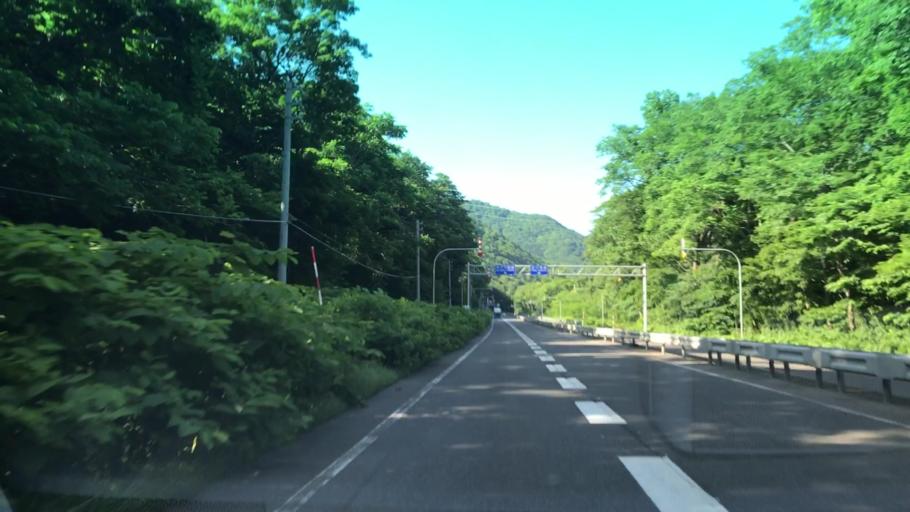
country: JP
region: Hokkaido
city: Iwanai
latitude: 43.0120
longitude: 140.6657
